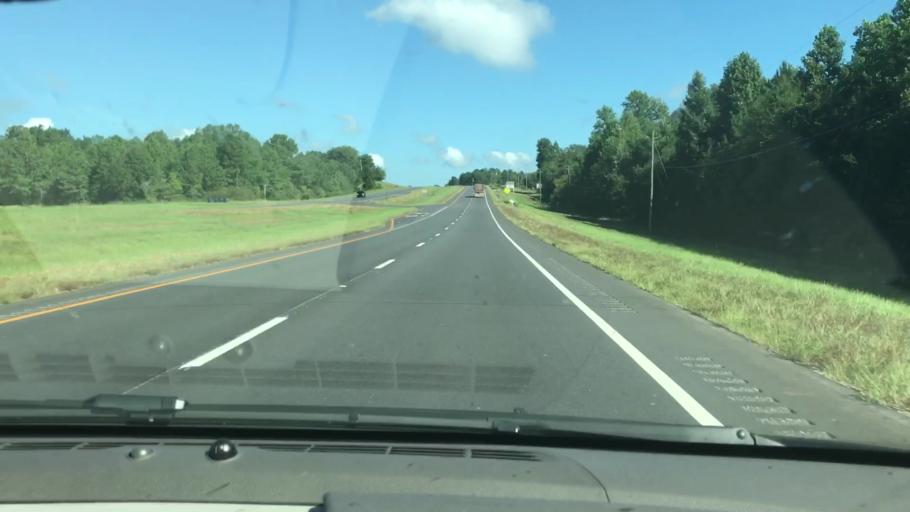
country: US
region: Alabama
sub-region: Barbour County
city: Eufaula
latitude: 32.0239
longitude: -85.1191
